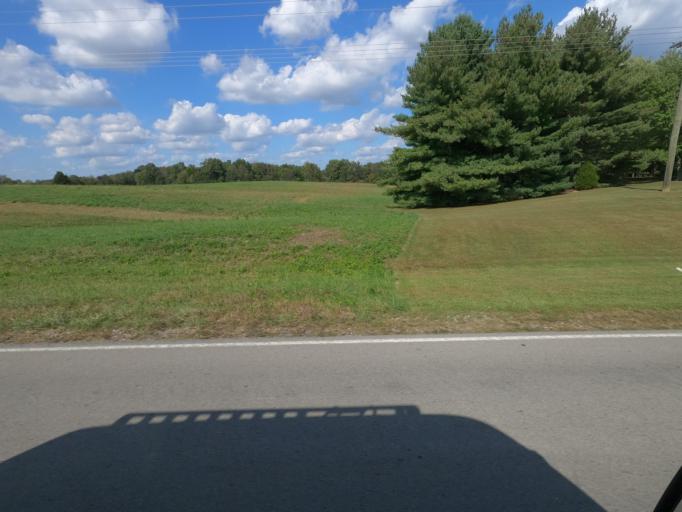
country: US
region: Illinois
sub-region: Massac County
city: Metropolis
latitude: 37.1909
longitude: -88.6830
